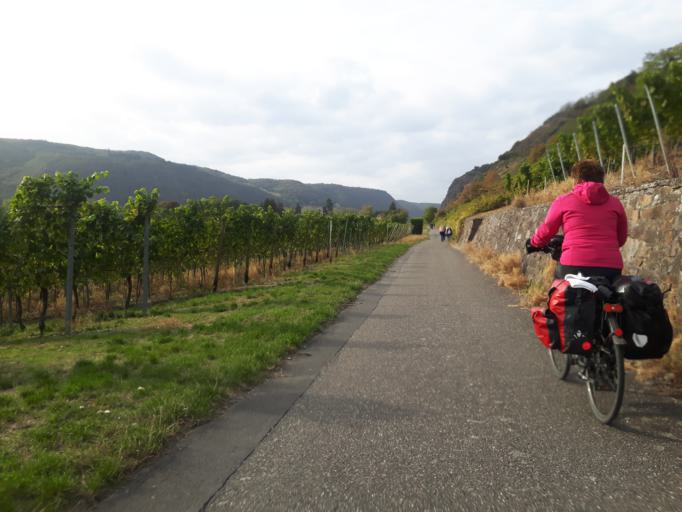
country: DE
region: Rheinland-Pfalz
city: Leutesdorf
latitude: 50.4631
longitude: 7.3699
